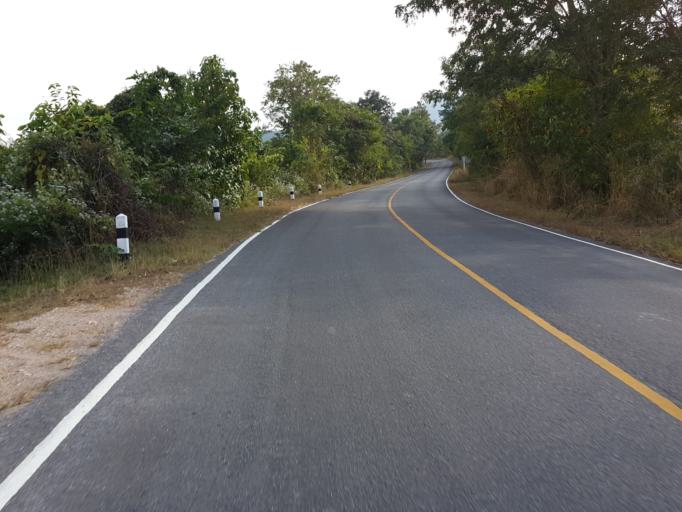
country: TH
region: Lamphun
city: Ban Hong
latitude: 18.2376
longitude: 98.9614
